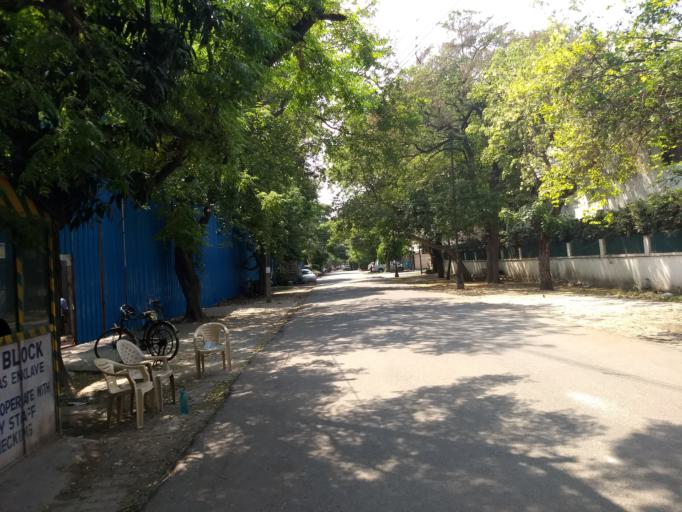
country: IN
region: NCT
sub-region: New Delhi
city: New Delhi
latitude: 28.5480
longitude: 77.2028
